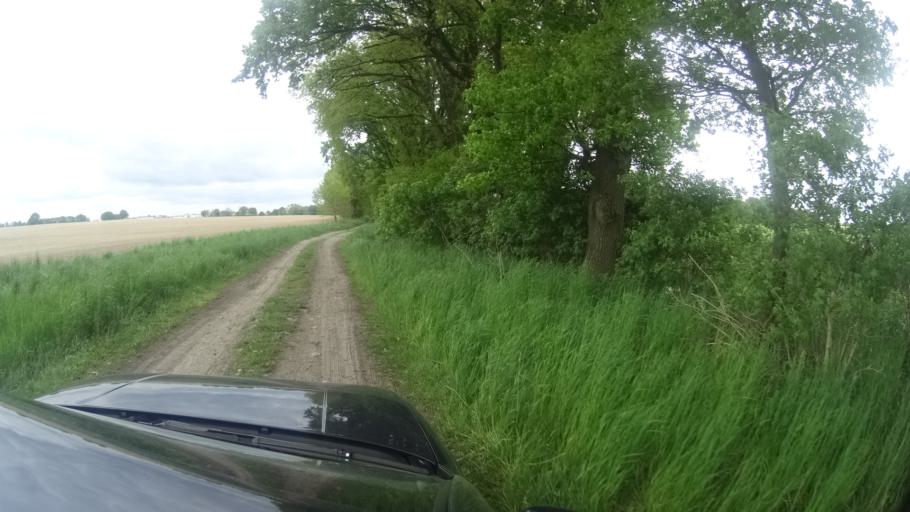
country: DE
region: Brandenburg
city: Neuruppin
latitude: 52.8991
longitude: 12.7799
